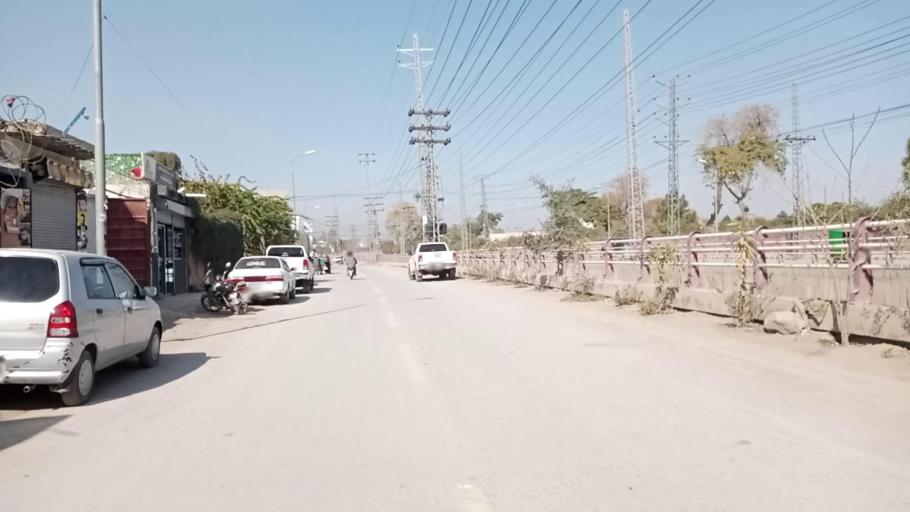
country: PK
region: Khyber Pakhtunkhwa
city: Peshawar
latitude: 33.9920
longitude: 71.4841
